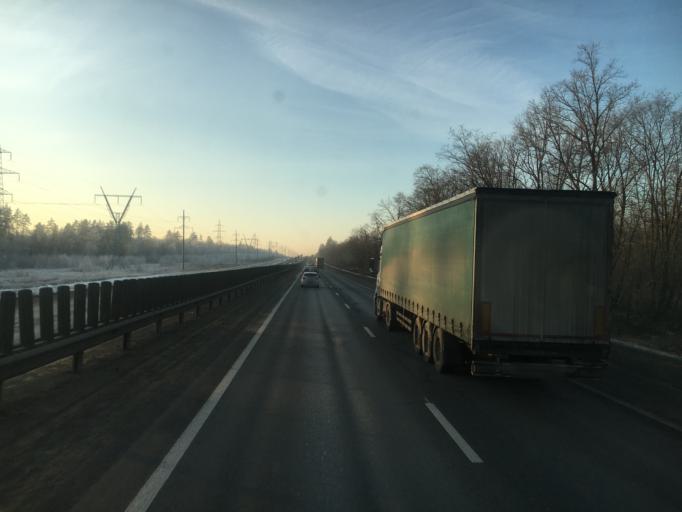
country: RU
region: Samara
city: Pribrezhnyy
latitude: 53.5150
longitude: 49.8828
